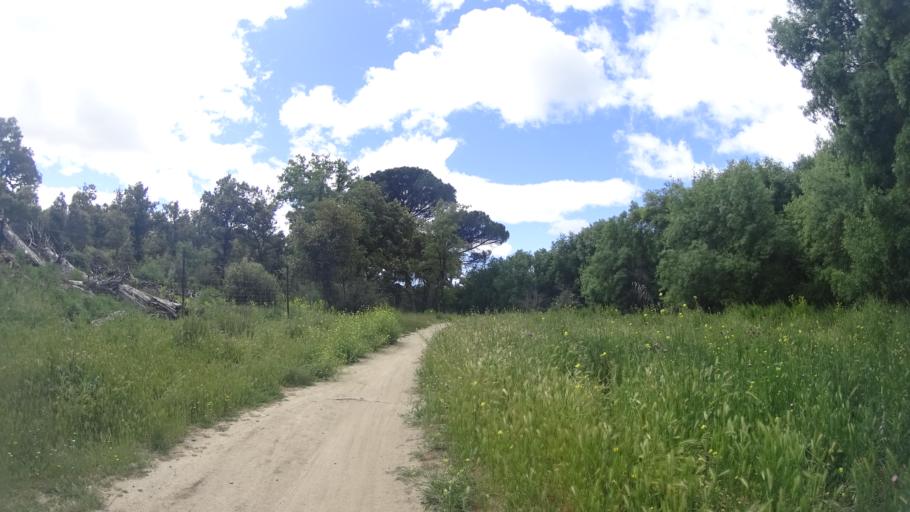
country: ES
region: Madrid
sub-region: Provincia de Madrid
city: Brunete
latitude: 40.3945
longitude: -3.9434
